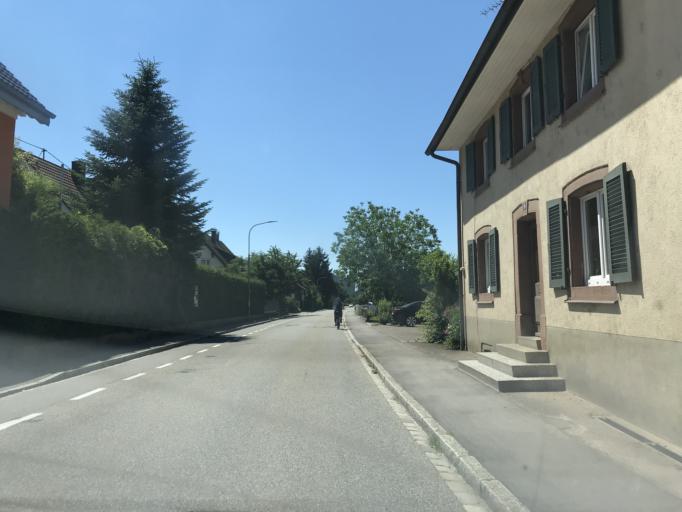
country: DE
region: Baden-Wuerttemberg
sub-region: Freiburg Region
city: Maulburg
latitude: 47.6577
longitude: 7.7989
